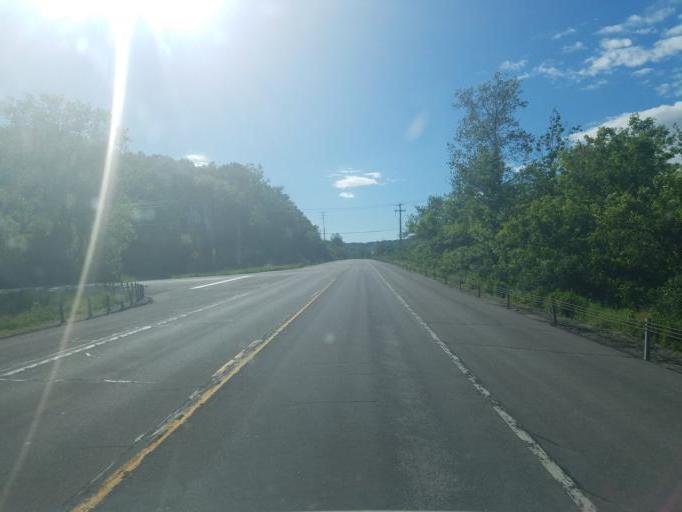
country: US
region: New York
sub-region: Herkimer County
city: Little Falls
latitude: 43.0330
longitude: -74.8301
